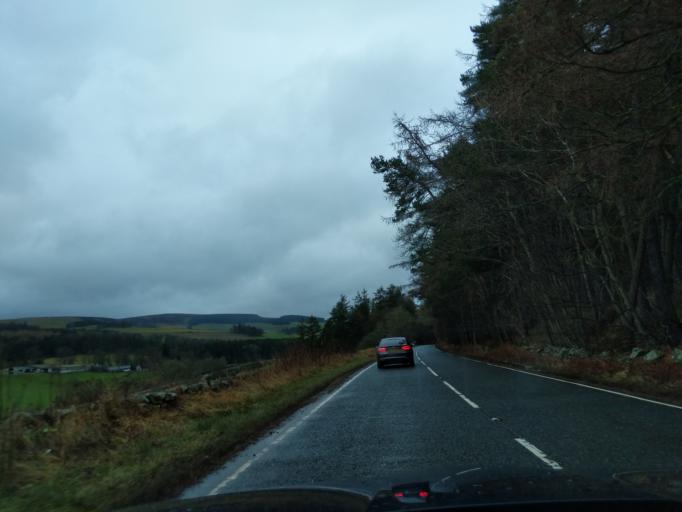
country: GB
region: Scotland
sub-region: The Scottish Borders
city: Galashiels
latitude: 55.6478
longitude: -2.8583
